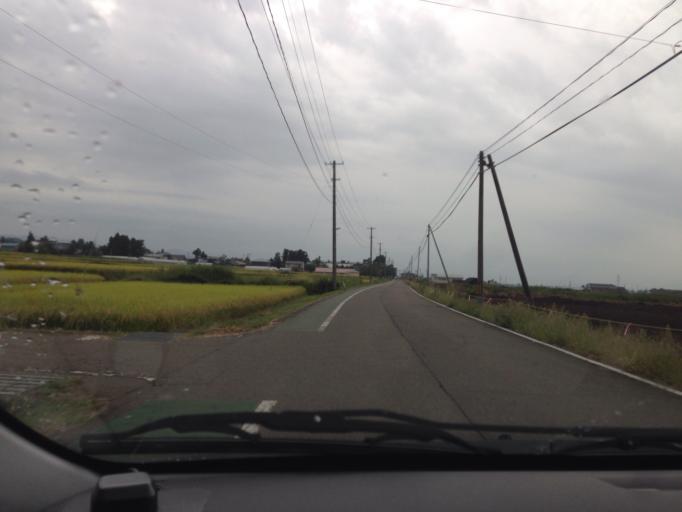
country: JP
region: Fukushima
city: Kitakata
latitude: 37.6075
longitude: 139.9140
